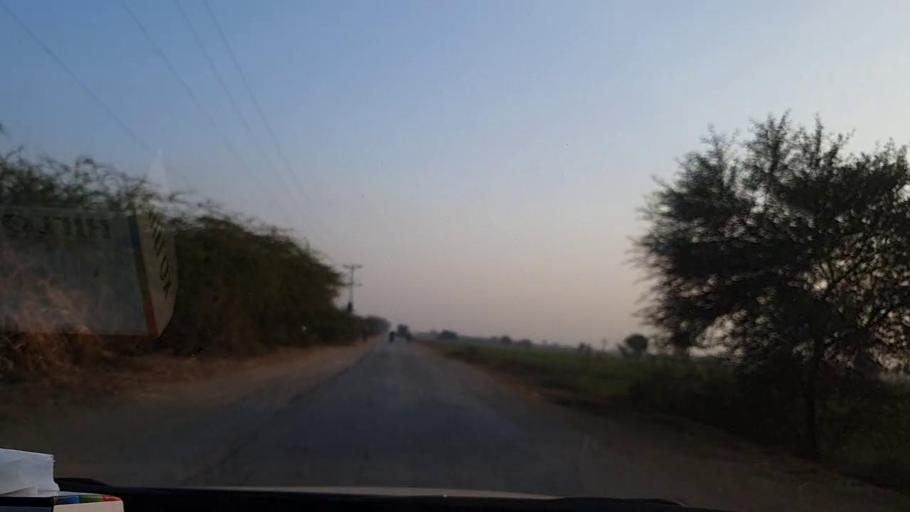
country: PK
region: Sindh
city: Tando Ghulam Ali
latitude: 25.1796
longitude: 68.9490
